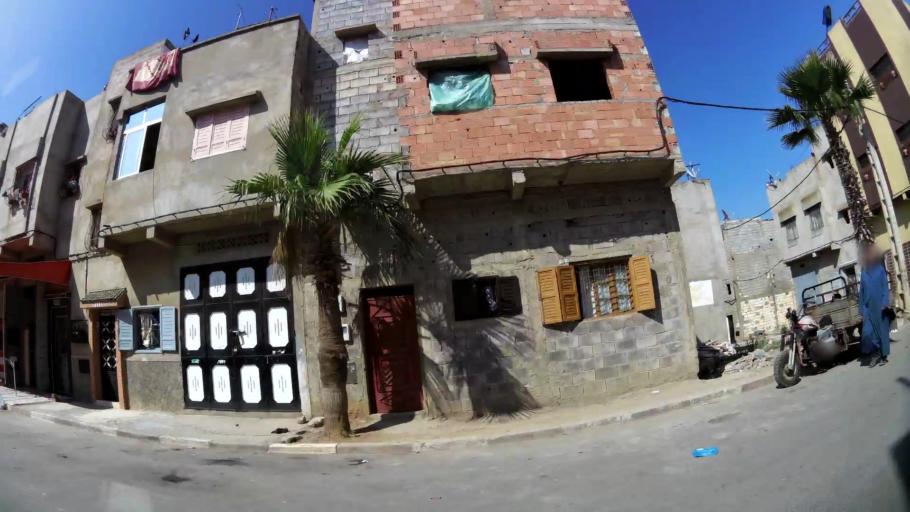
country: MA
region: Rabat-Sale-Zemmour-Zaer
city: Sale
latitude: 34.0676
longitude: -6.7719
